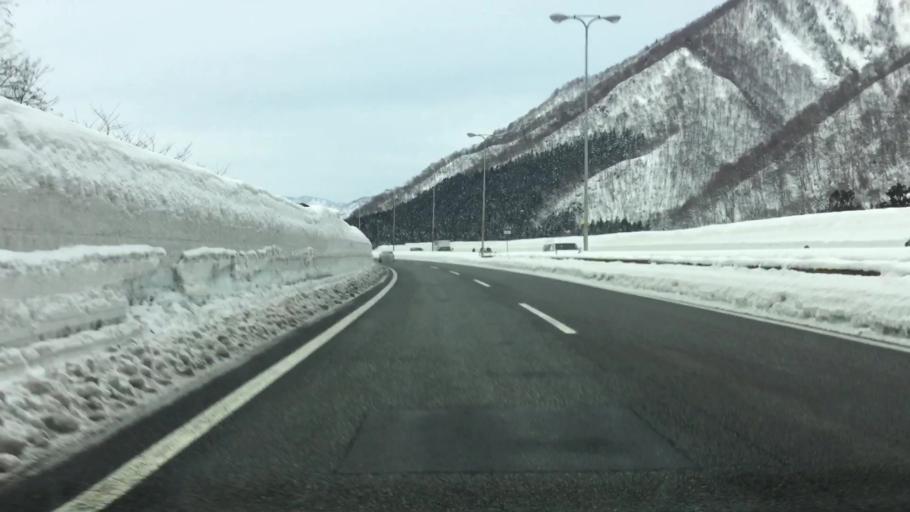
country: JP
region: Niigata
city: Shiozawa
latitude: 36.8729
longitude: 138.8643
